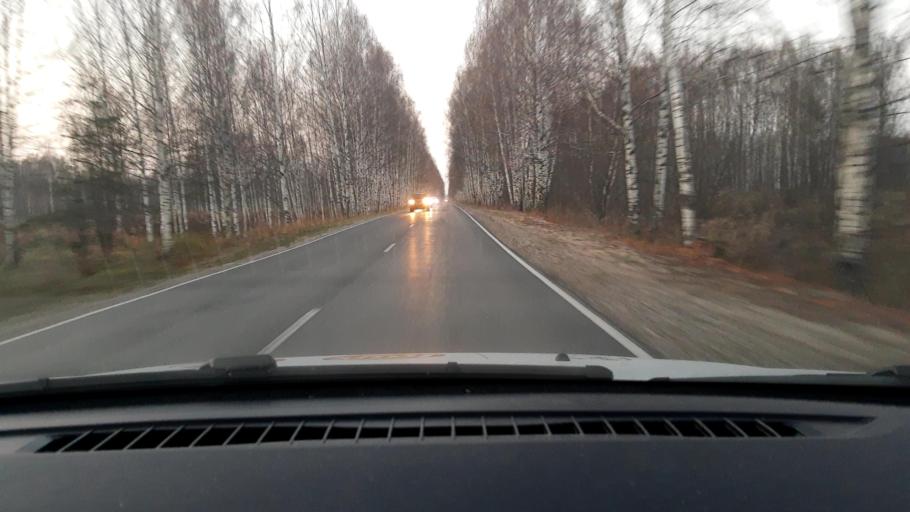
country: RU
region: Nizjnij Novgorod
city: Neklyudovo
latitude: 56.4840
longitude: 43.8675
